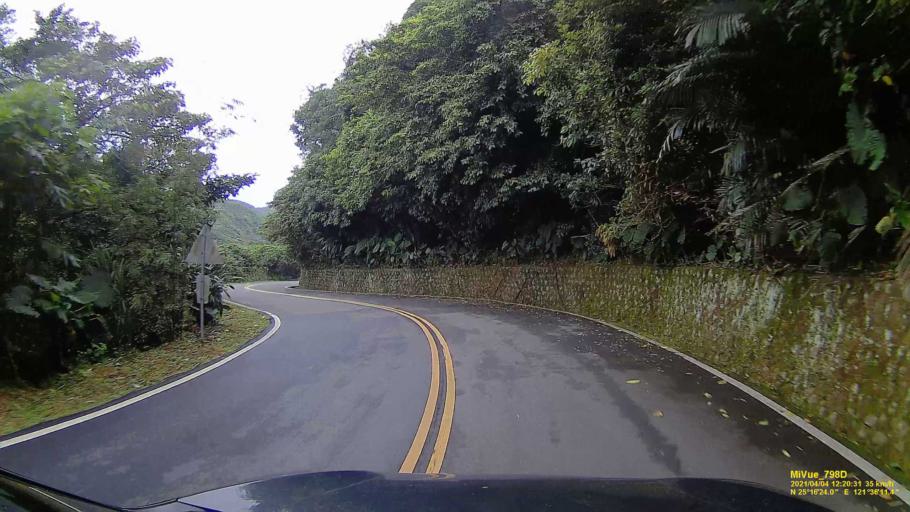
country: TW
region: Taiwan
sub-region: Keelung
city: Keelung
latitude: 25.2735
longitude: 121.6032
